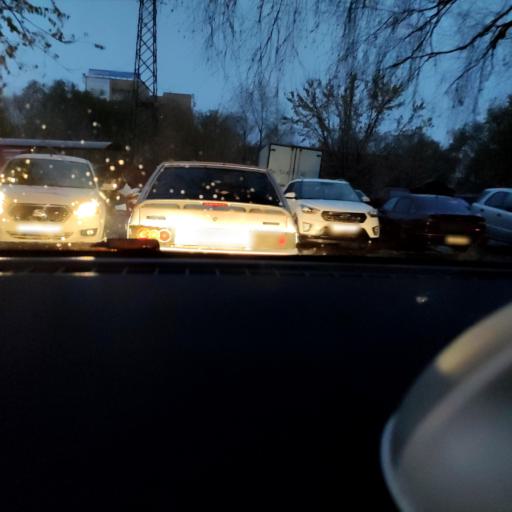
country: RU
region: Samara
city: Samara
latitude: 53.2440
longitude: 50.2514
